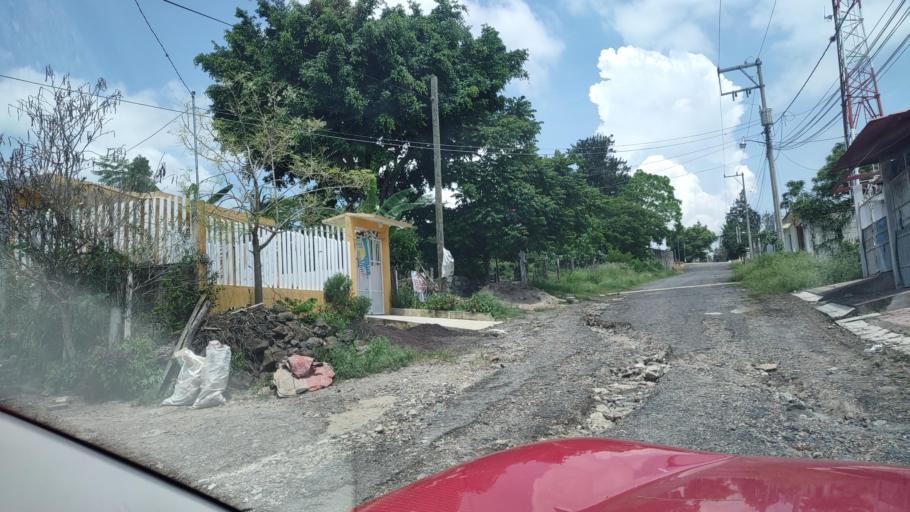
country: MX
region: Veracruz
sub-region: Emiliano Zapata
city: Dos Rios
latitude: 19.4896
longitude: -96.8125
